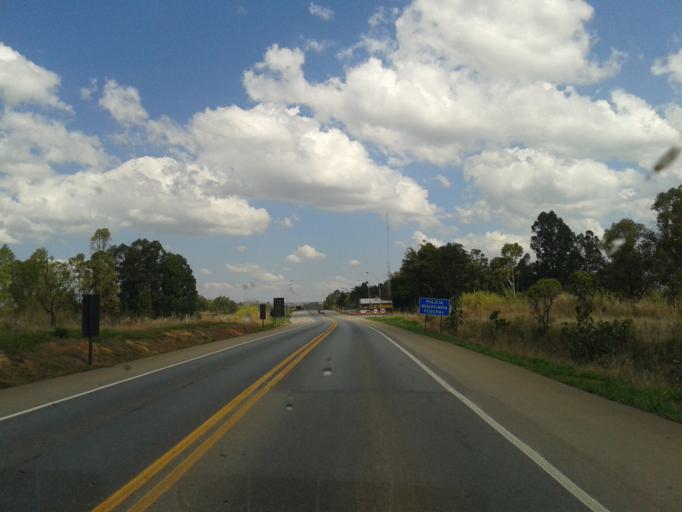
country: BR
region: Minas Gerais
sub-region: Campos Altos
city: Campos Altos
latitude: -19.6742
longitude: -46.0436
